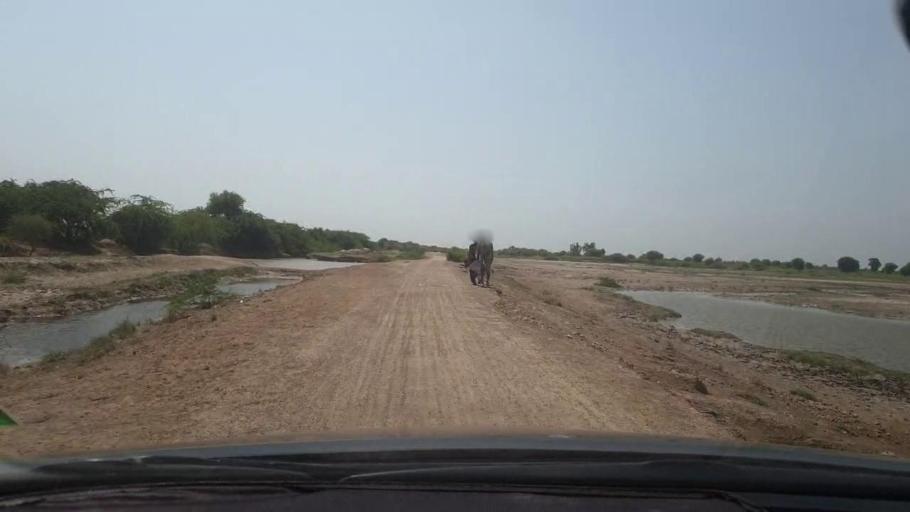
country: PK
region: Sindh
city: Tando Bago
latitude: 24.7944
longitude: 69.1796
